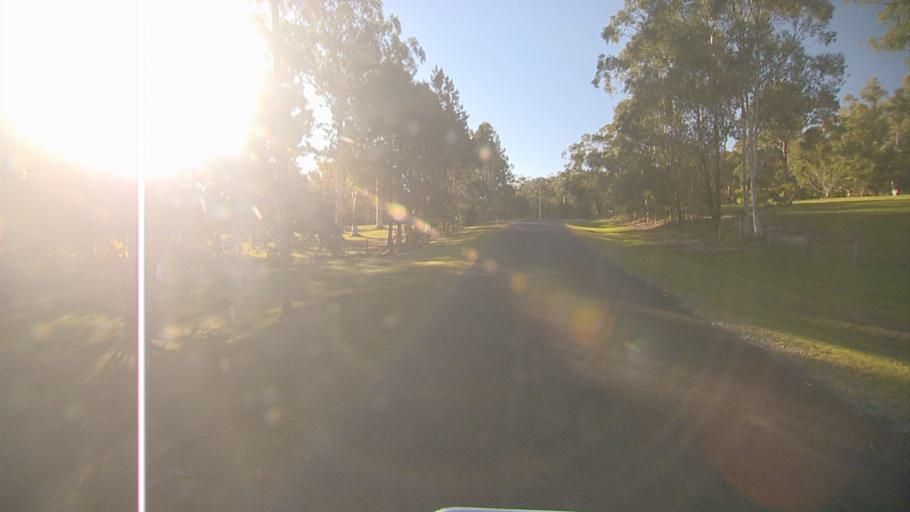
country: AU
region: Queensland
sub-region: Redland
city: Redland Bay
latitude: -27.6584
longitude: 153.2672
